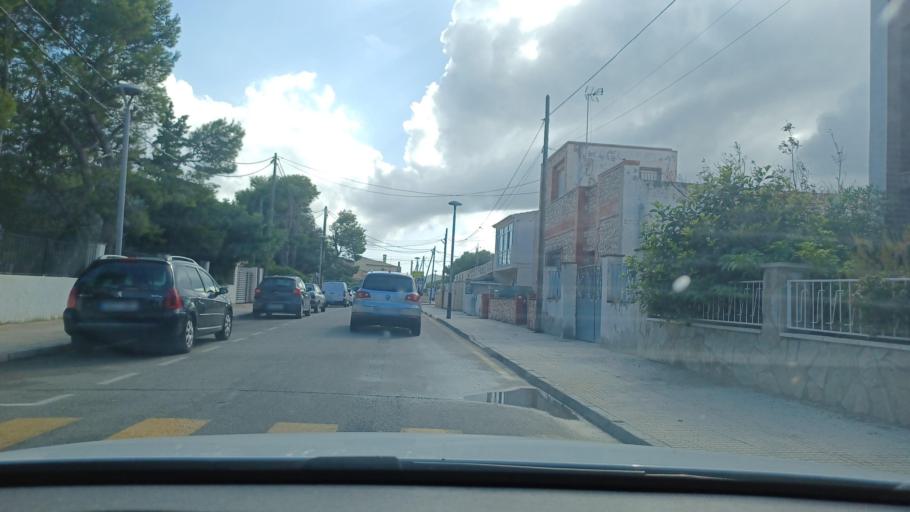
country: ES
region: Catalonia
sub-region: Provincia de Tarragona
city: Colldejou
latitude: 41.0019
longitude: 0.9308
